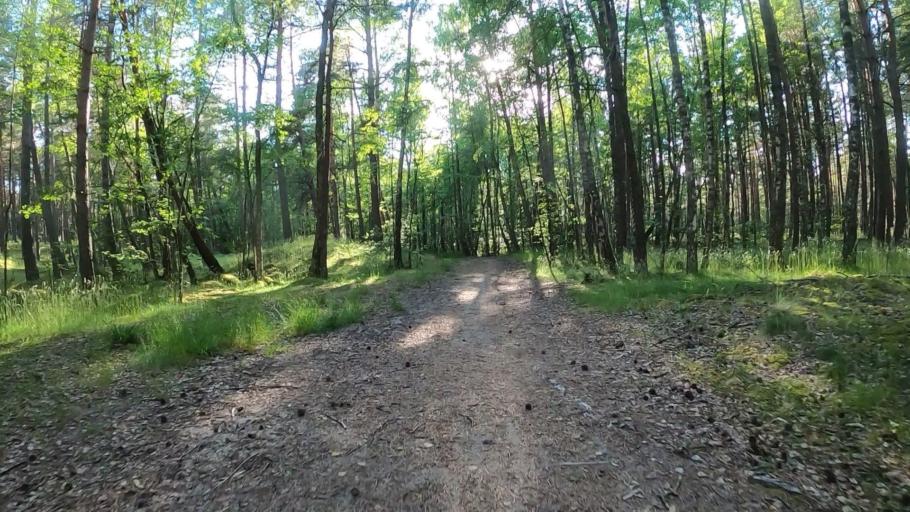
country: LV
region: Carnikava
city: Carnikava
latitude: 57.1389
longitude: 24.2418
